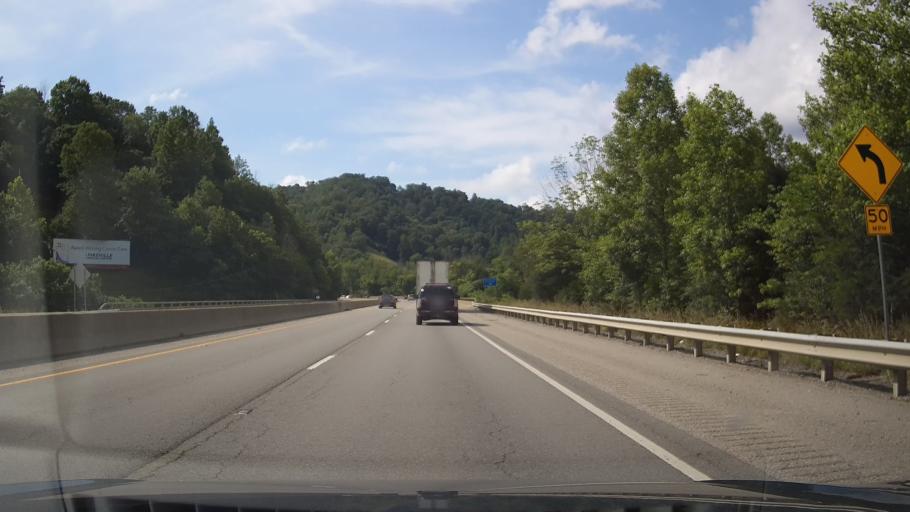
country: US
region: Kentucky
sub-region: Floyd County
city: Prestonsburg
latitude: 37.6202
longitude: -82.7241
